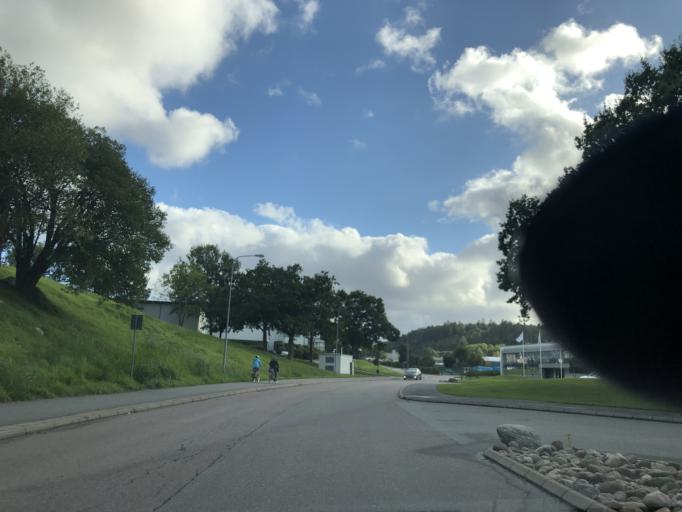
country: SE
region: Vaestra Goetaland
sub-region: Goteborg
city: Goeteborg
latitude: 57.7471
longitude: 11.9431
